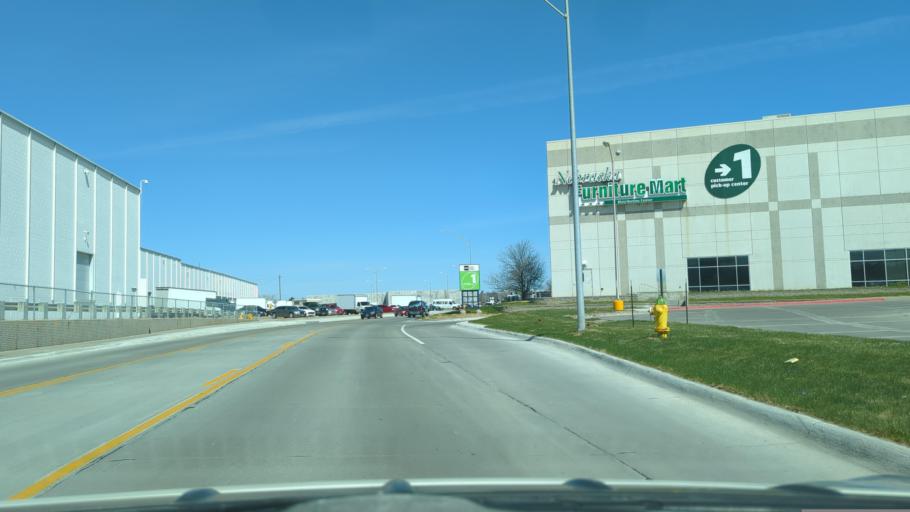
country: US
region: Nebraska
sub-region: Douglas County
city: Ralston
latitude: 41.2538
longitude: -96.0287
